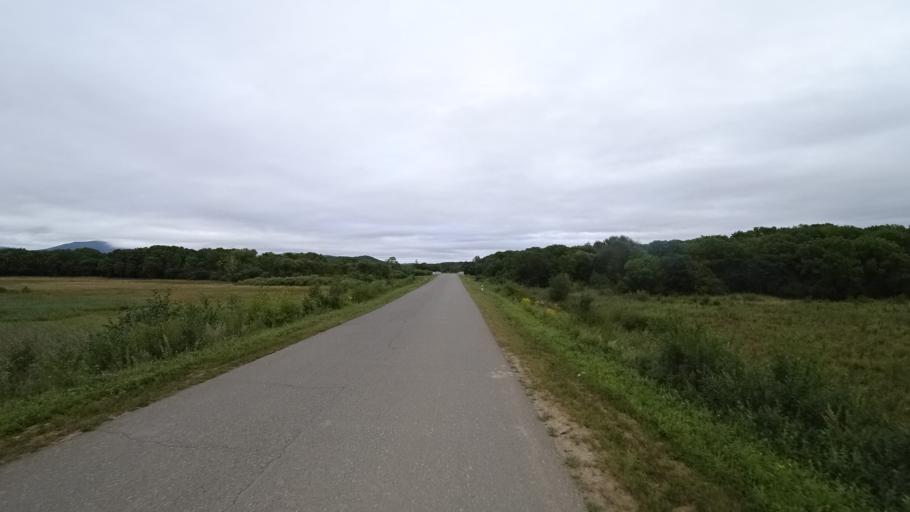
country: RU
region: Primorskiy
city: Rettikhovka
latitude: 44.1604
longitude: 132.7165
